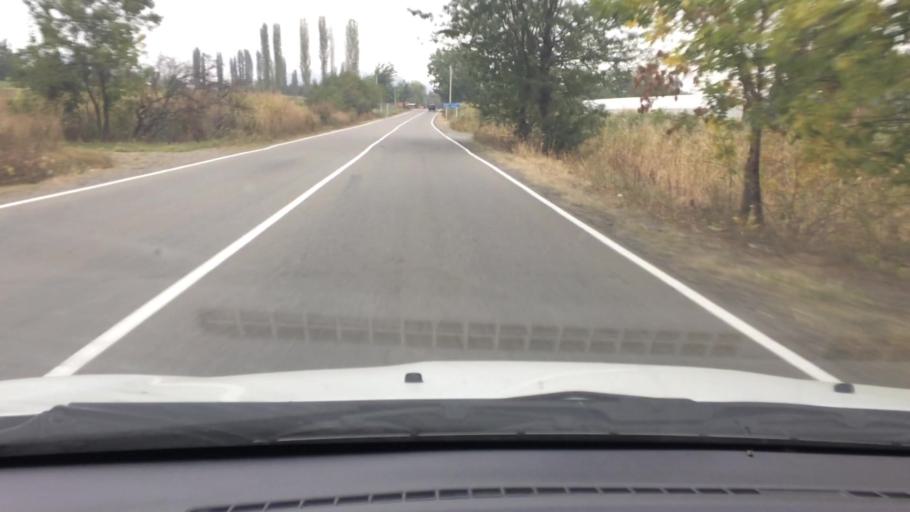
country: GE
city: Naghvarevi
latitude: 41.3190
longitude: 44.7953
